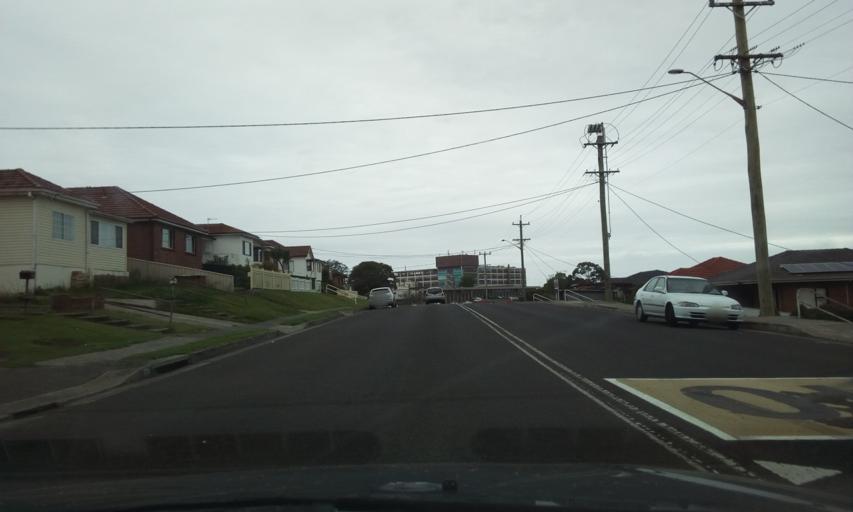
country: AU
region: New South Wales
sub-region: Wollongong
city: Lake Heights
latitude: -34.4826
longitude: 150.8795
